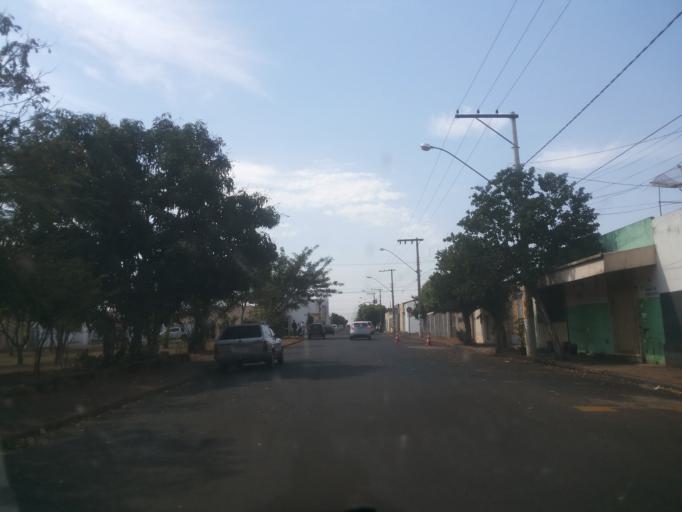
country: BR
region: Minas Gerais
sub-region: Ituiutaba
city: Ituiutaba
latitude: -18.9821
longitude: -49.4635
